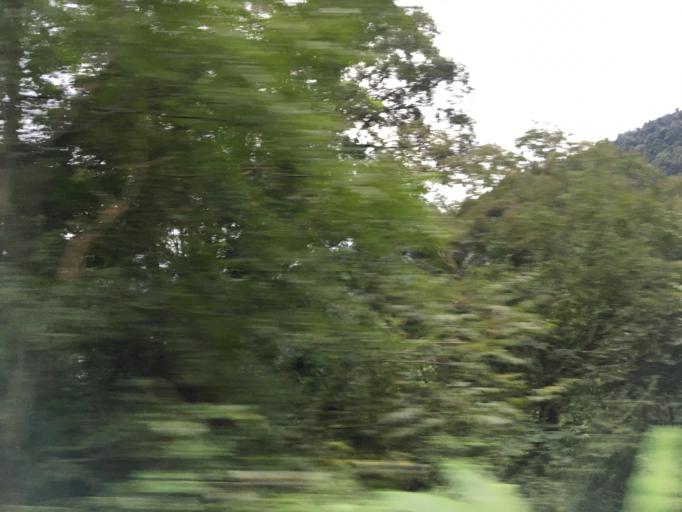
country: TW
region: Taiwan
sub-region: Yilan
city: Yilan
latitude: 24.5444
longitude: 121.5121
